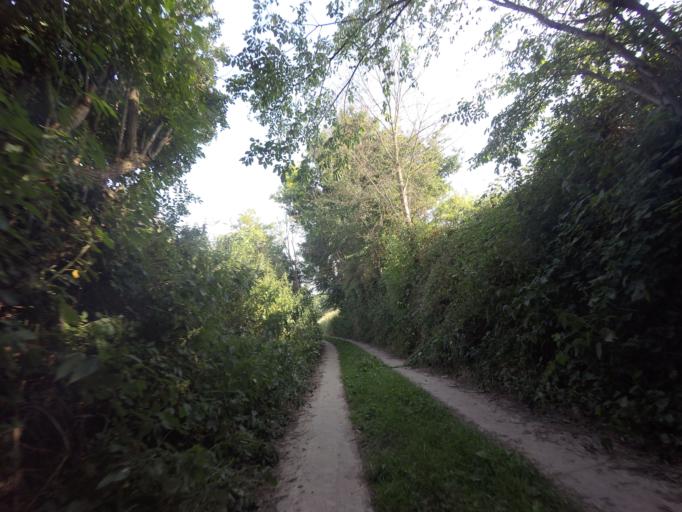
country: BE
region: Flanders
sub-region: Provincie Vlaams-Brabant
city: Grimbergen
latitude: 50.9192
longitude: 4.3724
